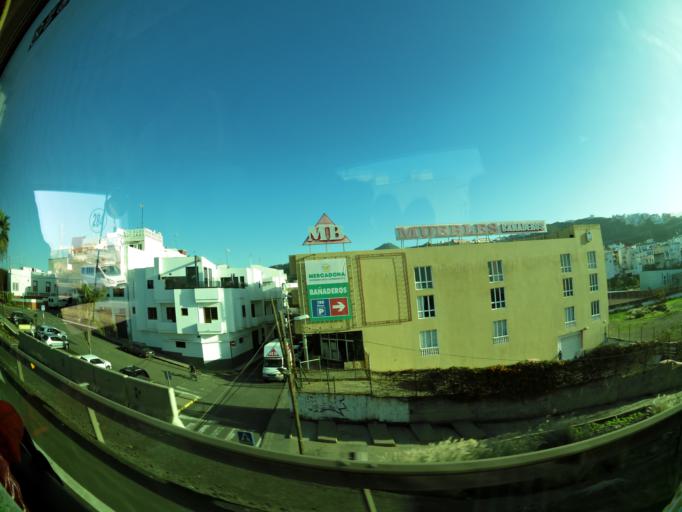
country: ES
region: Canary Islands
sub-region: Provincia de Las Palmas
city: Arucas
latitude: 28.1492
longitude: -15.5341
